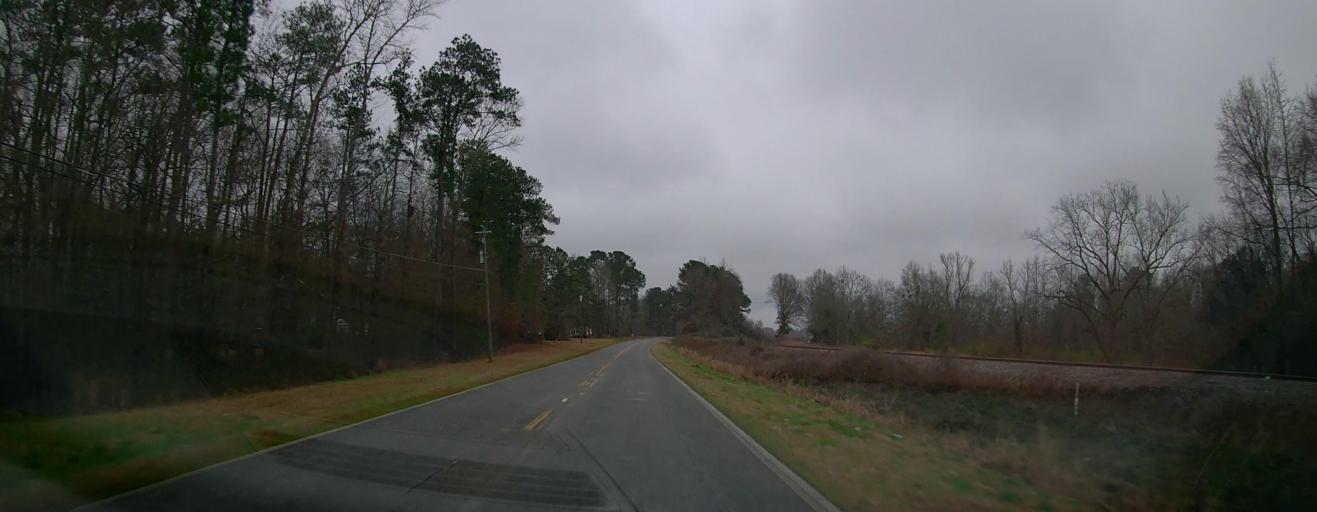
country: US
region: Georgia
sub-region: Lamar County
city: Barnesville
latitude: 33.1468
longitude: -84.1980
